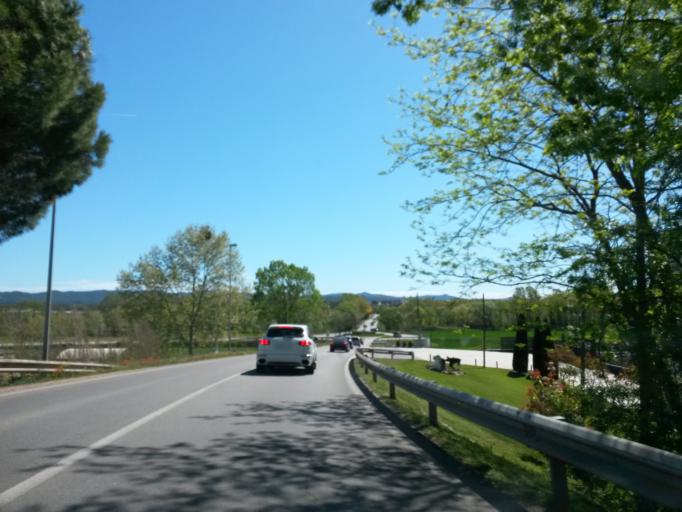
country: ES
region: Catalonia
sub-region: Provincia de Girona
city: Riudellots de la Selva
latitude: 41.8987
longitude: 2.8126
